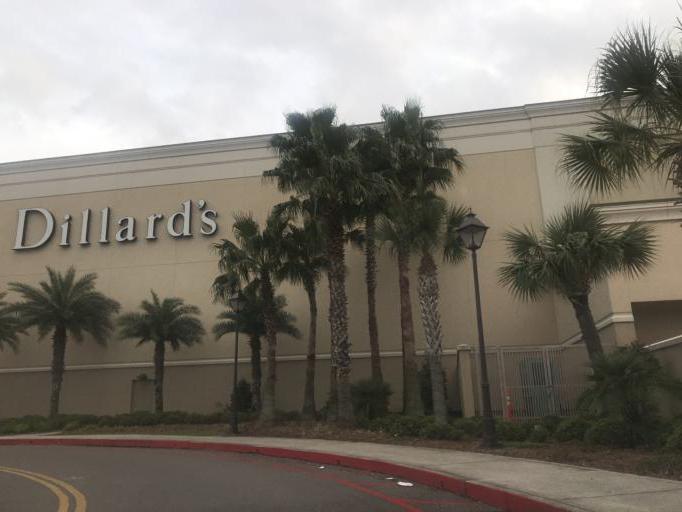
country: US
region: Louisiana
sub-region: Jefferson Parish
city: Metairie
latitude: 30.0078
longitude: -90.1578
